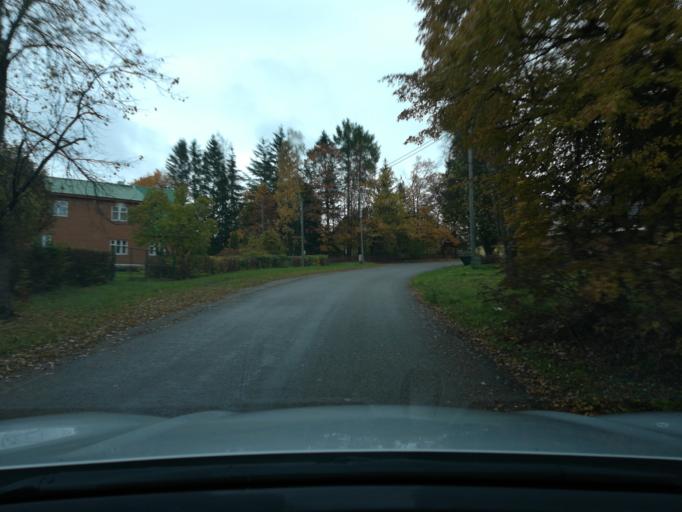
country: EE
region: Ida-Virumaa
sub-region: Johvi vald
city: Johvi
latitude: 59.2027
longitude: 27.5343
